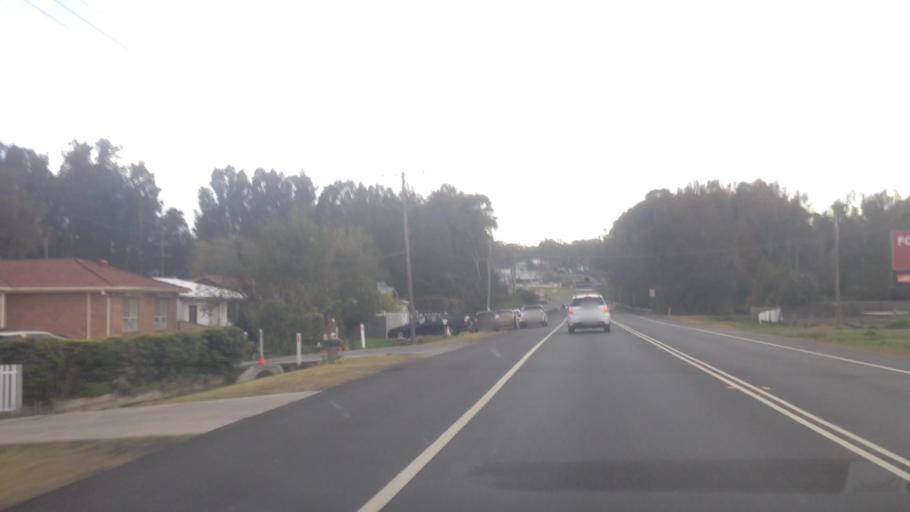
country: AU
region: New South Wales
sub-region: Wyong Shire
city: Tuggerawong
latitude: -33.2636
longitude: 151.4773
